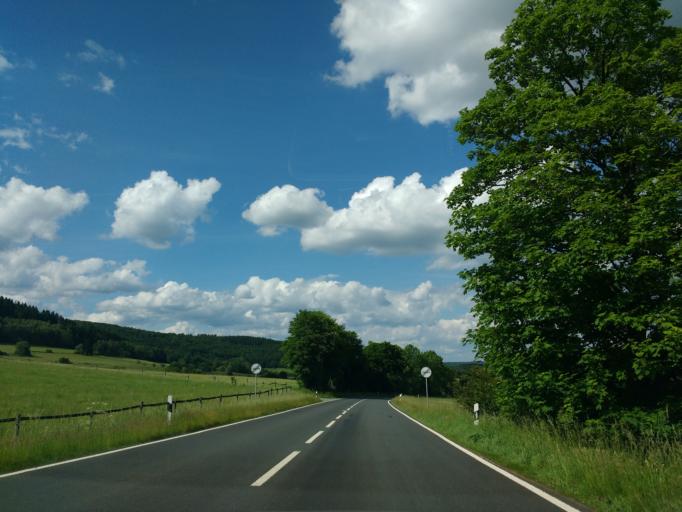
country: DE
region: Hesse
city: Hatzfeld
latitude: 50.9547
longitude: 8.5710
